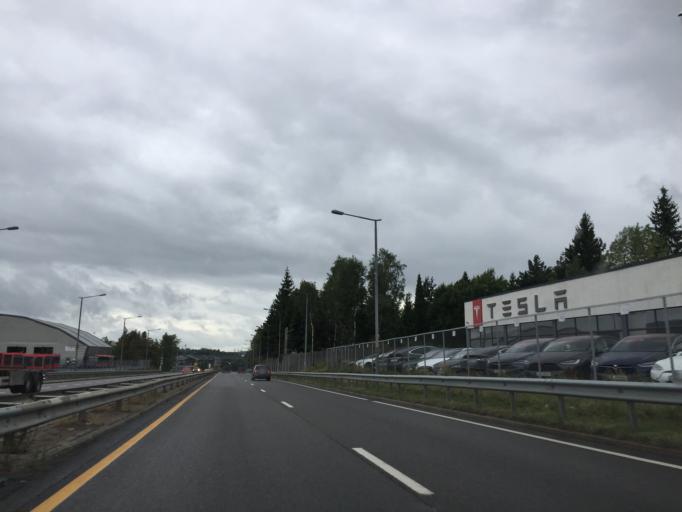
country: NO
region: Akershus
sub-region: Lorenskog
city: Kjenn
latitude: 59.9530
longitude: 10.8891
